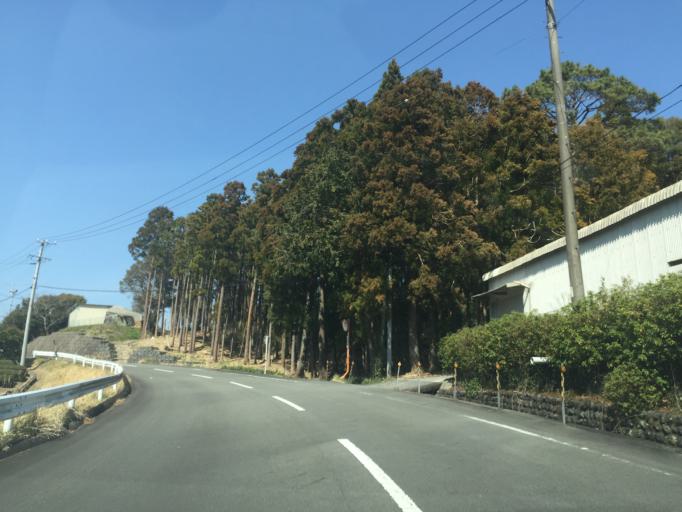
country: JP
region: Shizuoka
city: Kanaya
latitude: 34.8023
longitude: 138.1249
